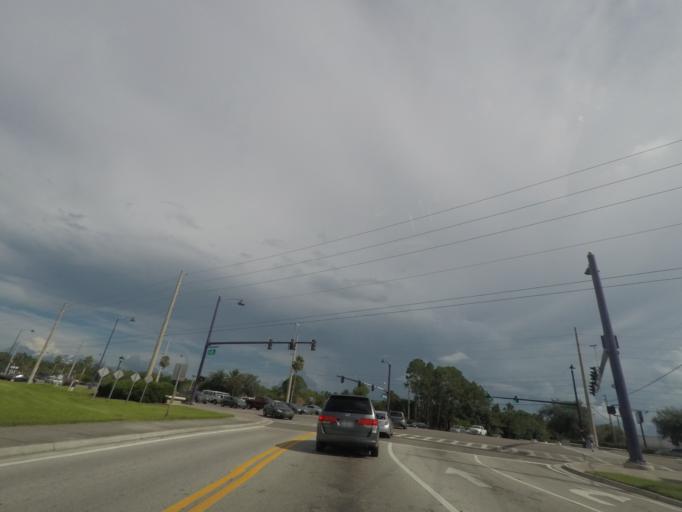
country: US
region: Florida
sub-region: Osceola County
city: Kissimmee
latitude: 28.3042
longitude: -81.4577
